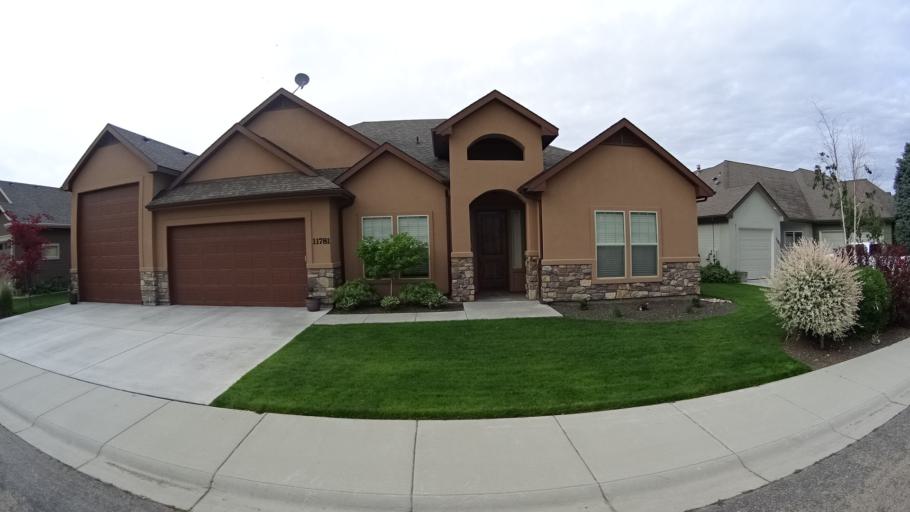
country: US
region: Idaho
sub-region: Ada County
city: Star
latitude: 43.6875
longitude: -116.5002
